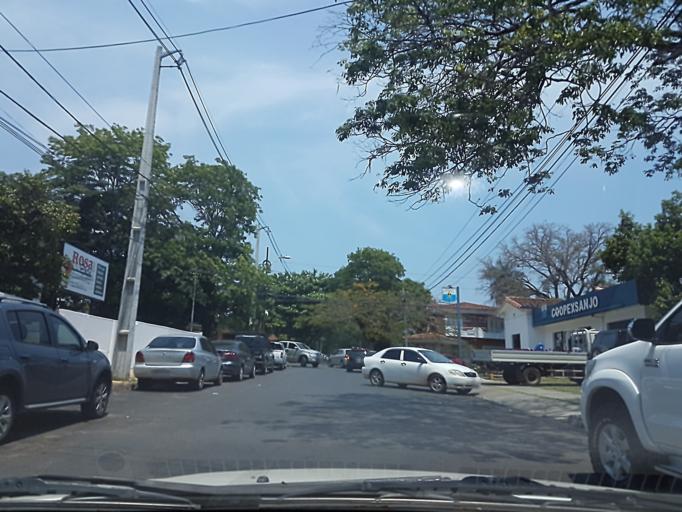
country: PY
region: Asuncion
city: Asuncion
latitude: -25.2889
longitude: -57.6070
